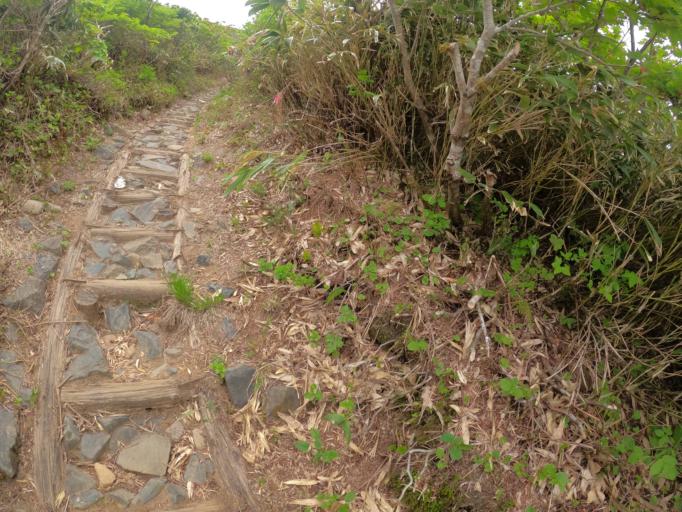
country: JP
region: Iwate
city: Ichinoseki
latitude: 38.9623
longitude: 140.7912
